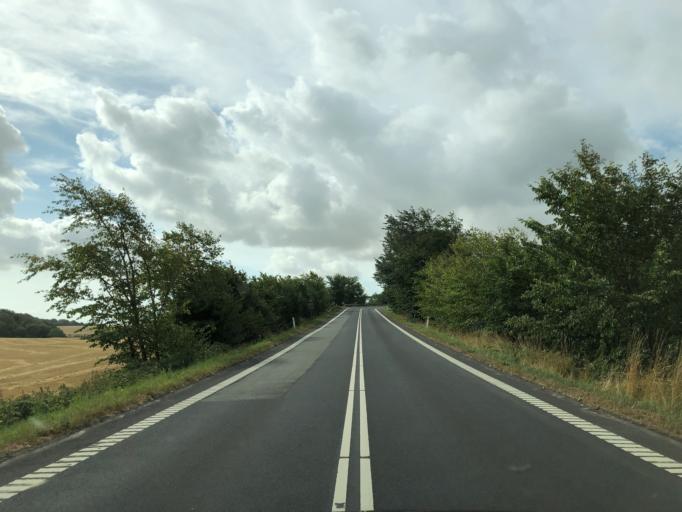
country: DK
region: South Denmark
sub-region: Kolding Kommune
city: Kolding
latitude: 55.5184
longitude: 9.5378
